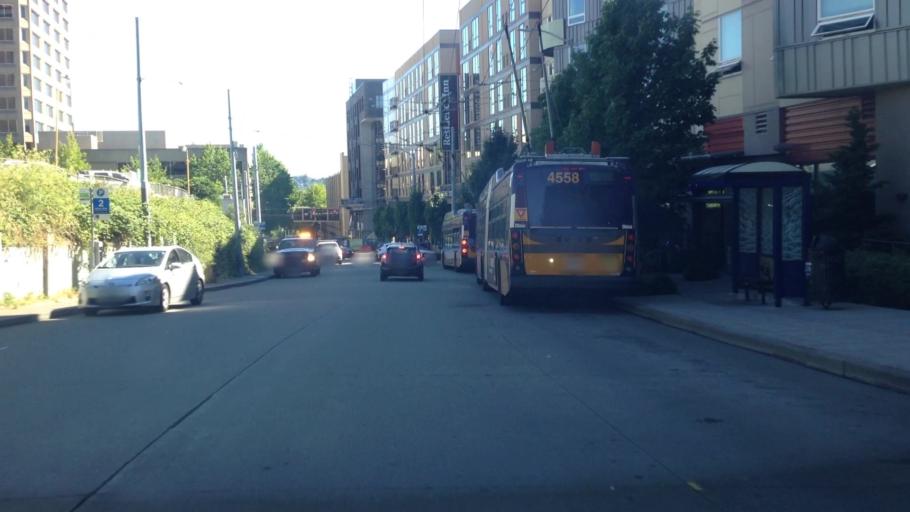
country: US
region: Washington
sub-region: King County
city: Seattle
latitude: 47.6626
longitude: -122.3153
